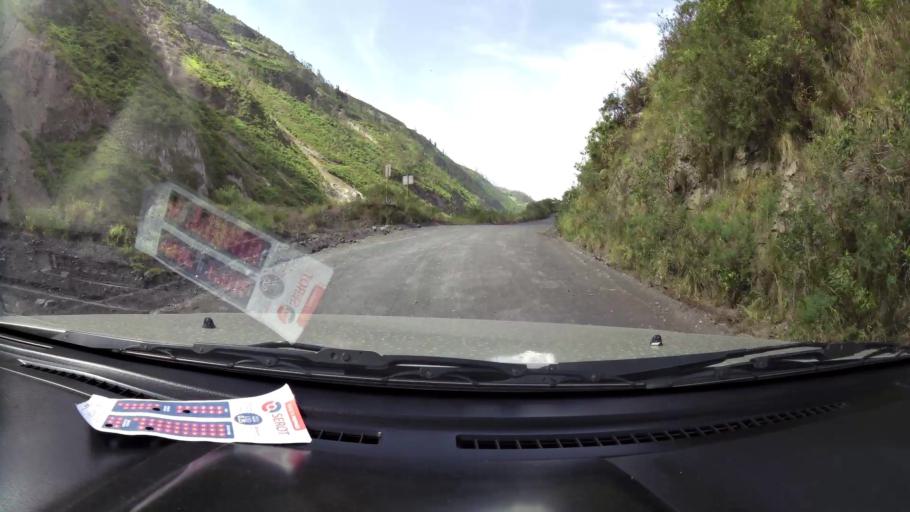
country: EC
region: Tungurahua
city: Banos
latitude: -1.4725
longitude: -78.5125
